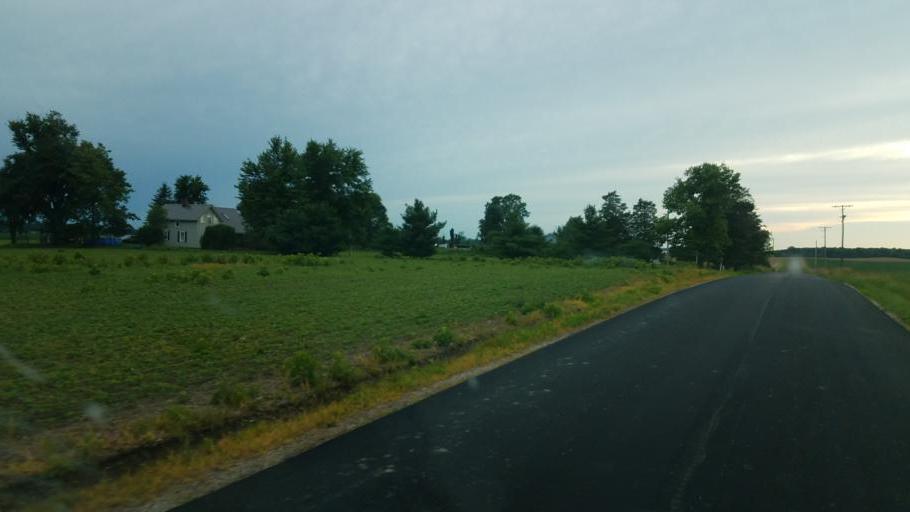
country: US
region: Ohio
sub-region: Huron County
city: Greenwich
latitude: 40.9537
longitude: -82.4827
